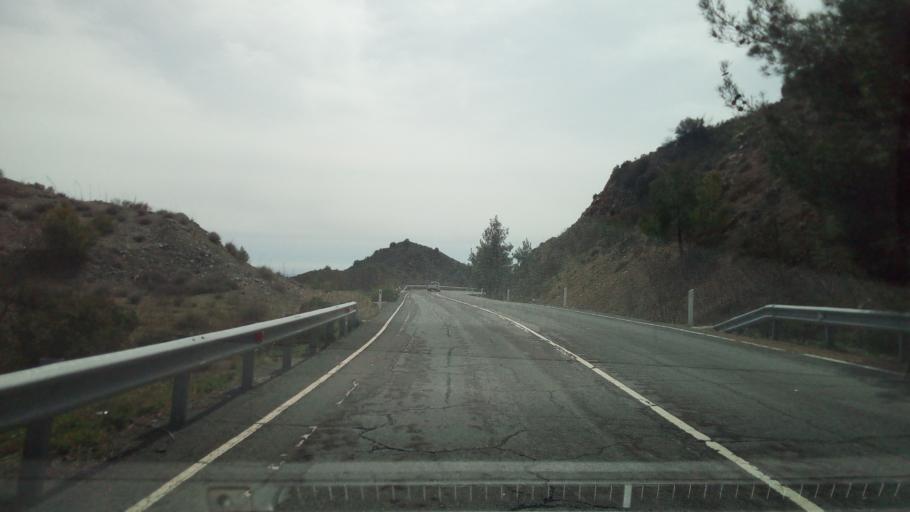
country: CY
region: Limassol
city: Pelendri
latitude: 34.8774
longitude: 32.9449
